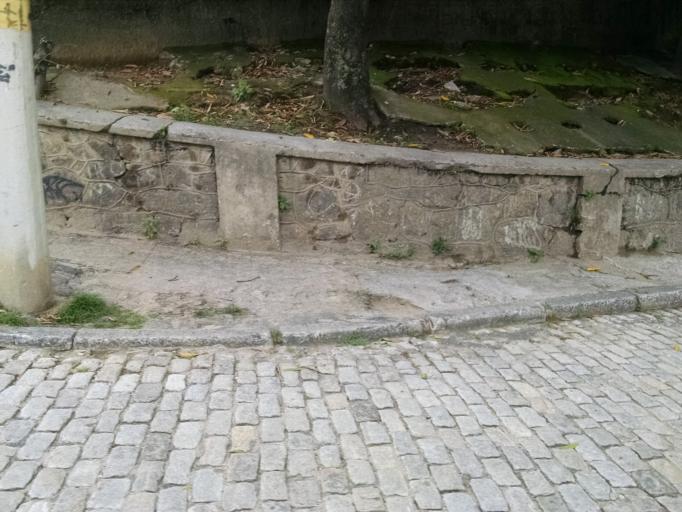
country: BR
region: Rio de Janeiro
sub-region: Rio De Janeiro
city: Rio de Janeiro
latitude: -22.9157
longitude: -43.1813
